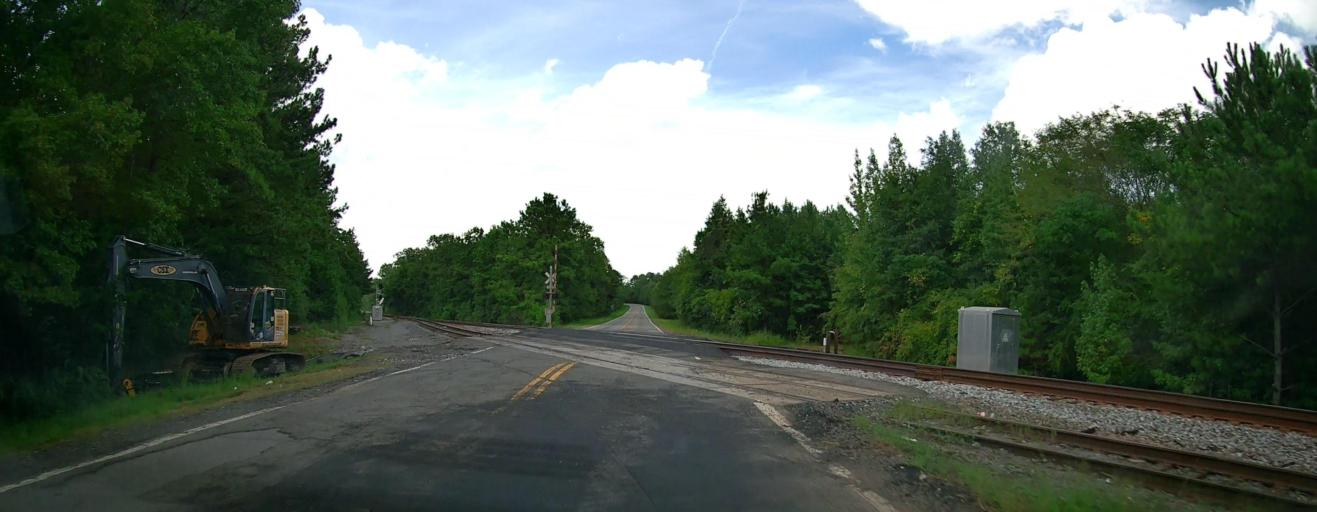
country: US
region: Georgia
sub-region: Talbot County
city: Talbotton
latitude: 32.6351
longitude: -84.4927
